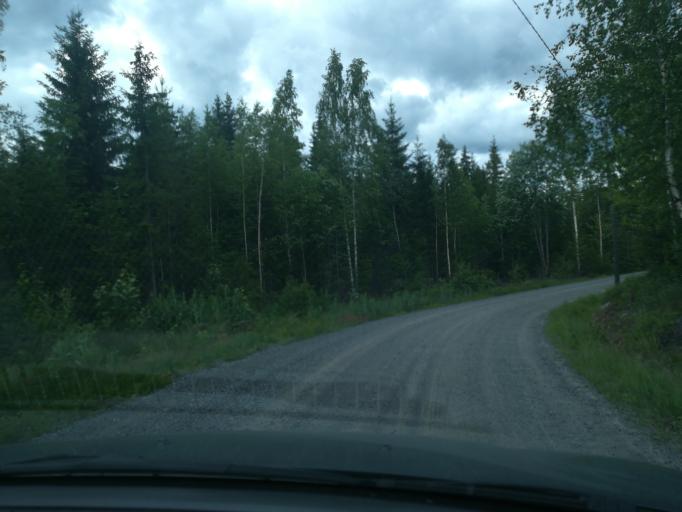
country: FI
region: Southern Savonia
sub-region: Mikkeli
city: Mikkeli
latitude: 61.6658
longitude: 27.1186
